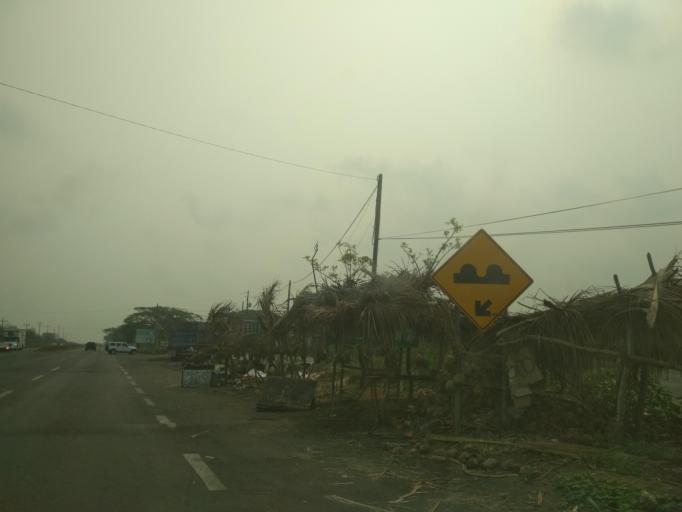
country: MX
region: Veracruz
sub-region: Veracruz
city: Delfino Victoria (Santa Fe)
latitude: 19.2089
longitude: -96.2611
